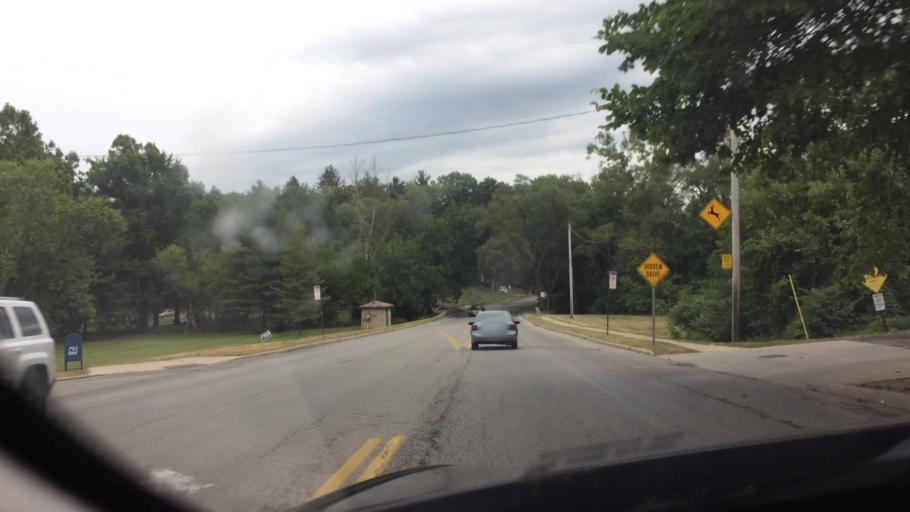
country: US
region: Ohio
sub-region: Lucas County
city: Ottawa Hills
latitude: 41.6521
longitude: -83.6409
